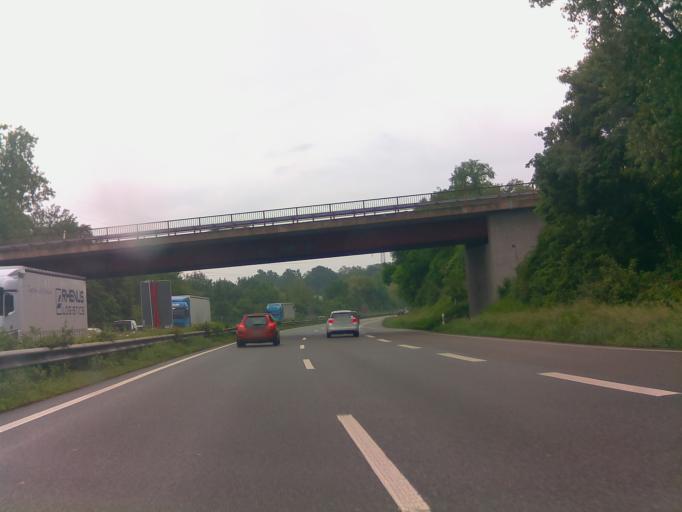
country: DE
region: Rheinland-Pfalz
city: Germersheim
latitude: 49.2227
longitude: 8.3558
